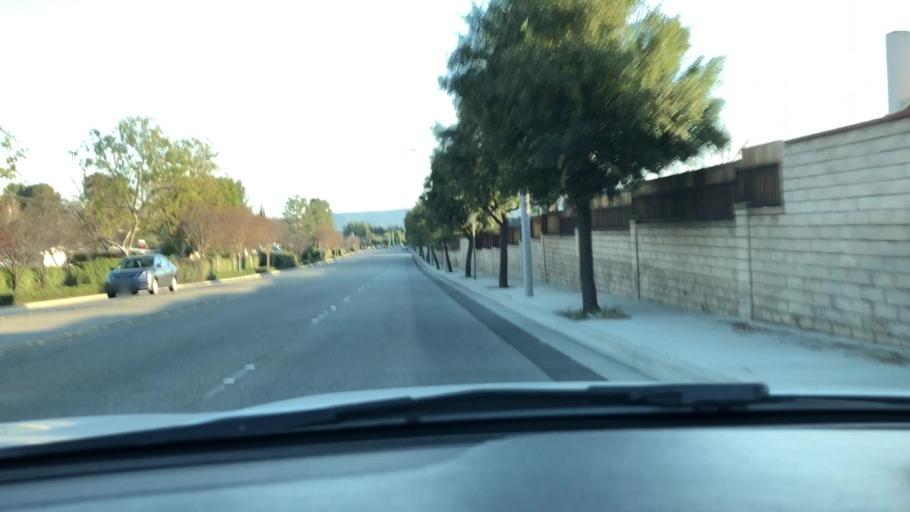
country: US
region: California
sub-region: Los Angeles County
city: Santa Clarita
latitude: 34.4550
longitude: -118.5351
